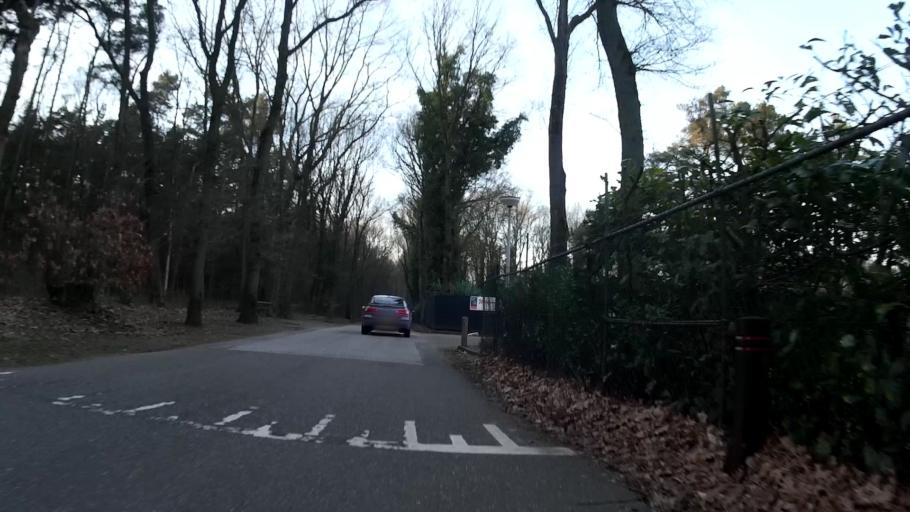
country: NL
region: Utrecht
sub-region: Gemeente Veenendaal
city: Veenendaal
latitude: 51.9993
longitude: 5.5432
